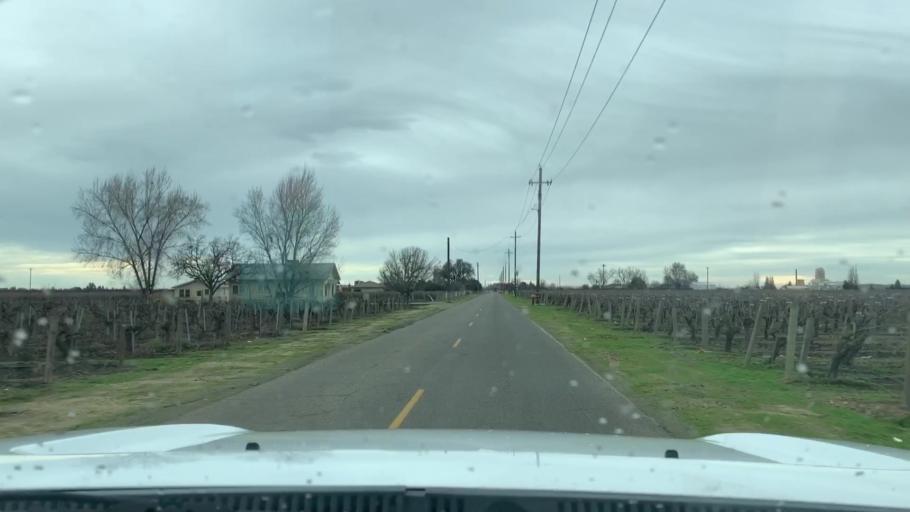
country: US
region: California
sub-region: Fresno County
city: Selma
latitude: 36.5567
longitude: -119.5751
